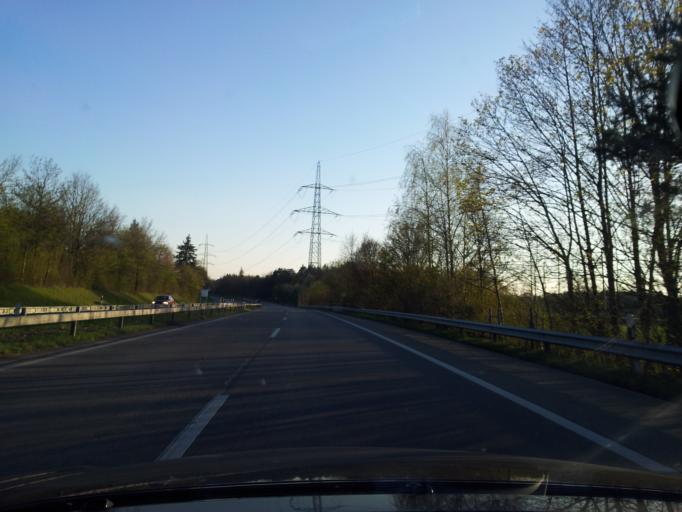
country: CH
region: Bern
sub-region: Seeland District
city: Lyss
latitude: 47.0819
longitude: 7.2946
